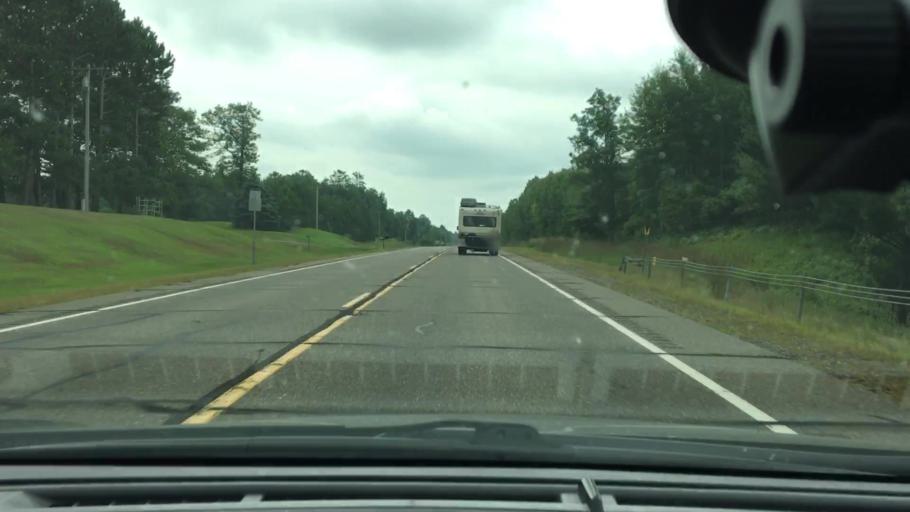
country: US
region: Minnesota
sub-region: Crow Wing County
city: Crosby
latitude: 46.4306
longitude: -93.8736
